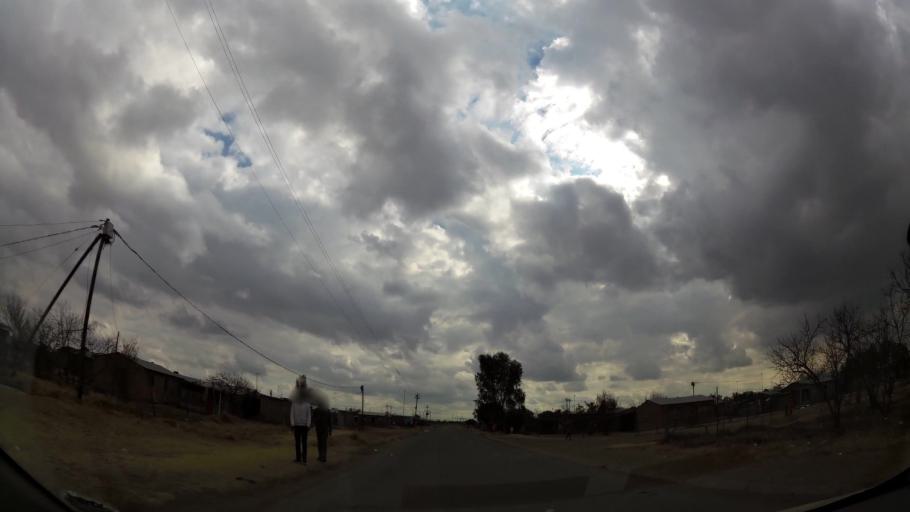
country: ZA
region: Orange Free State
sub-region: Fezile Dabi District Municipality
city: Sasolburg
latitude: -26.8535
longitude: 27.8715
